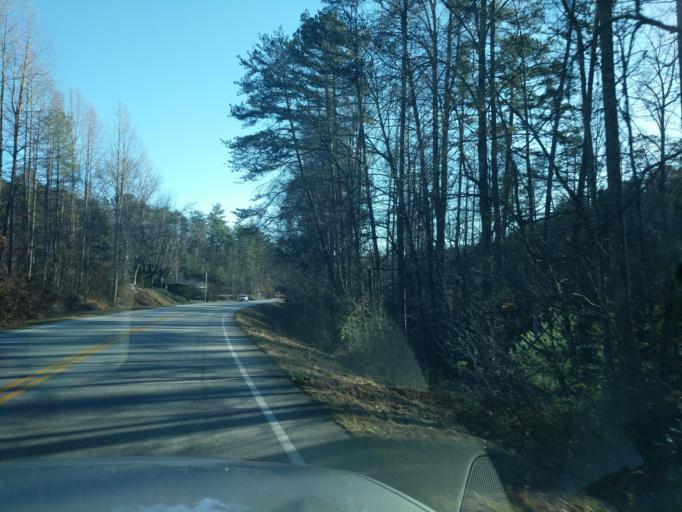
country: US
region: Georgia
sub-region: Rabun County
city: Clayton
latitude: 34.8216
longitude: -83.3198
